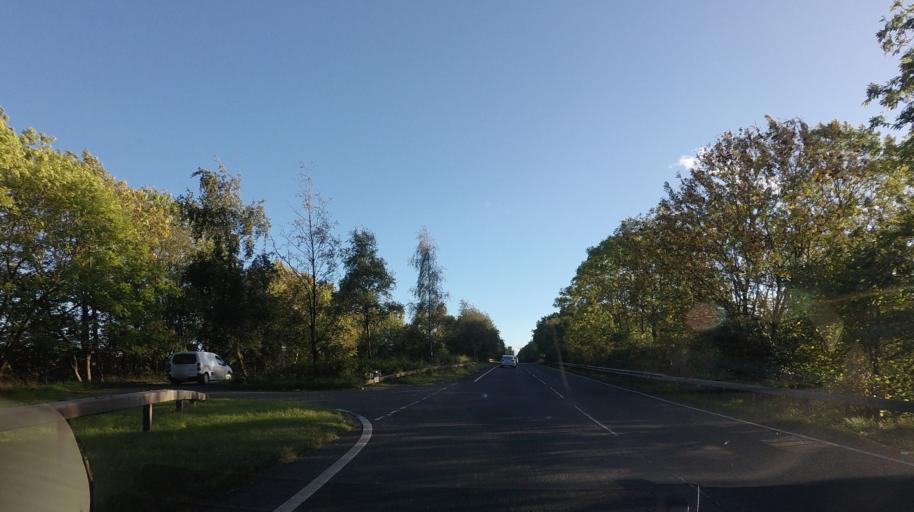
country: GB
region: Scotland
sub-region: Falkirk
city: Polmont
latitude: 55.9802
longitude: -3.6835
